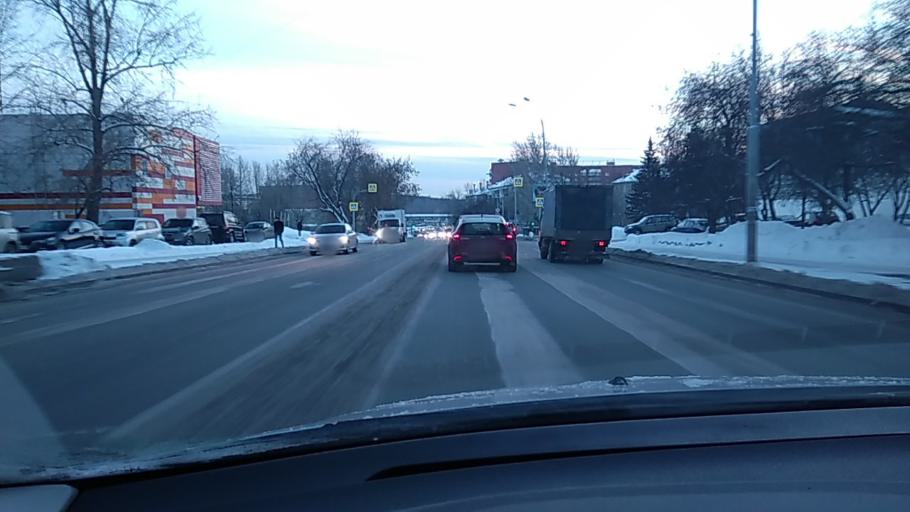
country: RU
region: Sverdlovsk
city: Yekaterinburg
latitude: 56.8228
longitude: 60.6390
